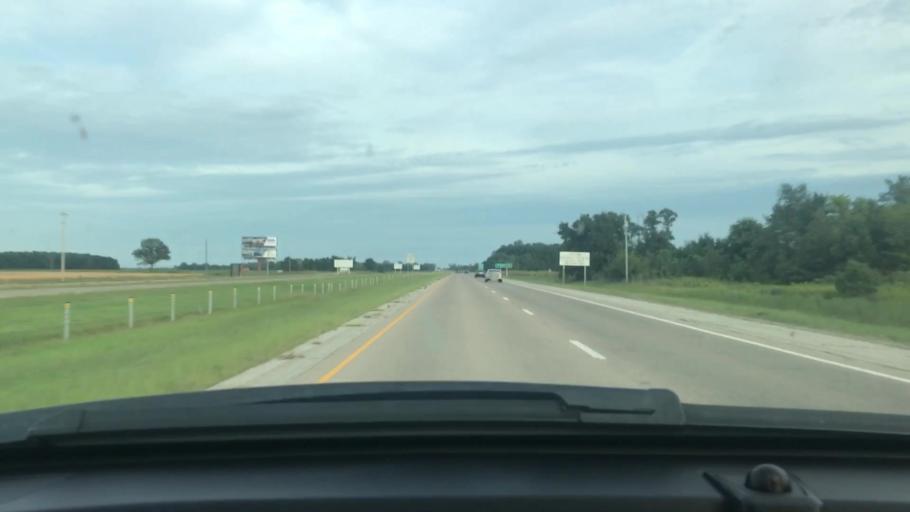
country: US
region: Arkansas
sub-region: Craighead County
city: Bay
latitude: 35.7930
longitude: -90.6127
